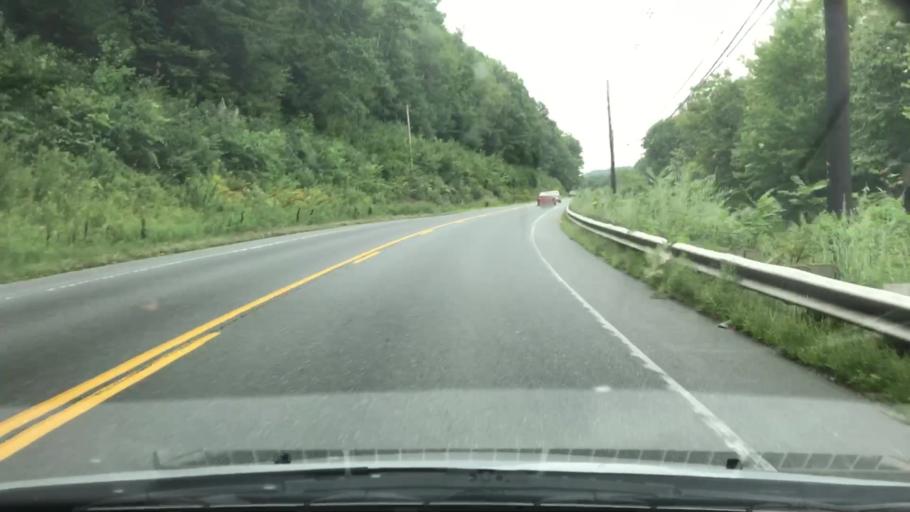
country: US
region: New Hampshire
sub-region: Grafton County
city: Woodsville
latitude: 44.1240
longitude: -72.0338
